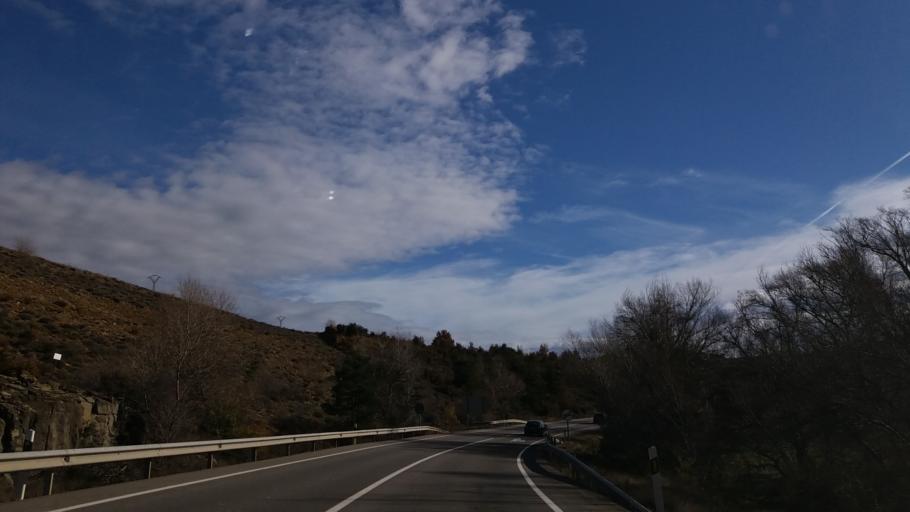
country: ES
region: Aragon
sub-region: Provincia de Huesca
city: Arguis
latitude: 42.4080
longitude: -0.3877
